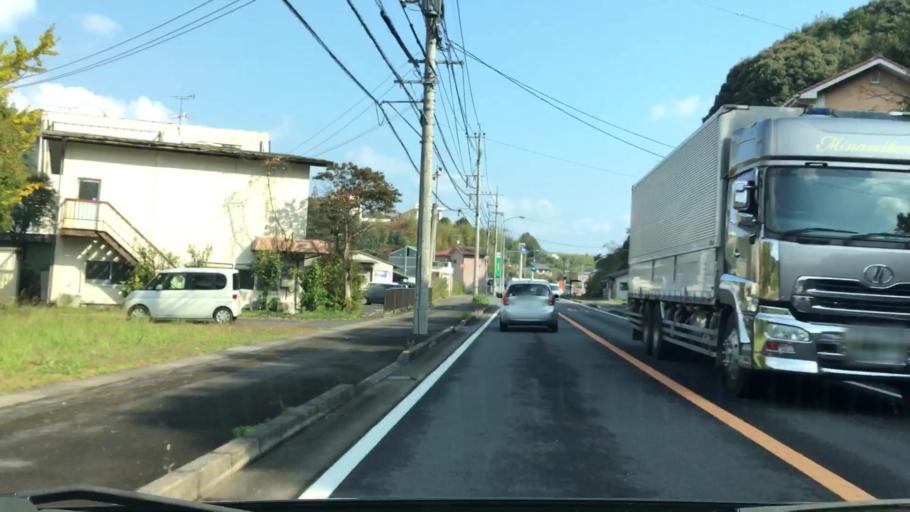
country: JP
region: Nagasaki
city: Togitsu
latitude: 32.9869
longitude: 129.7719
